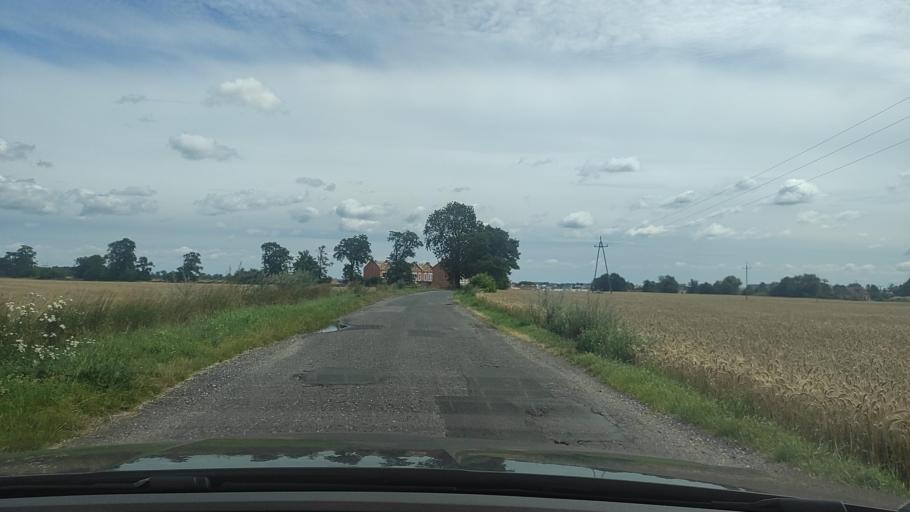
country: PL
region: Greater Poland Voivodeship
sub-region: Powiat poznanski
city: Kostrzyn
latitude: 52.4090
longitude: 17.1868
